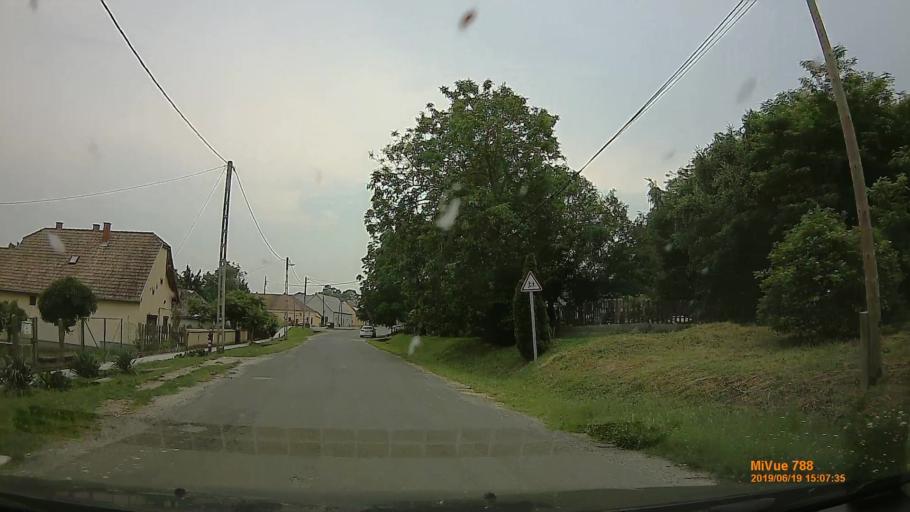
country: HU
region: Baranya
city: Szigetvar
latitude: 46.0911
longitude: 17.8046
